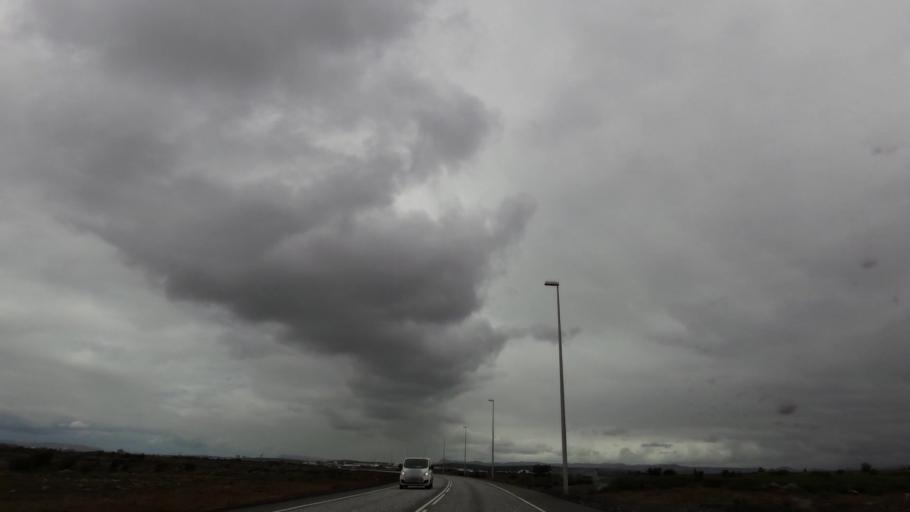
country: IS
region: Capital Region
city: Alftanes
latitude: 64.0909
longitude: -21.9836
